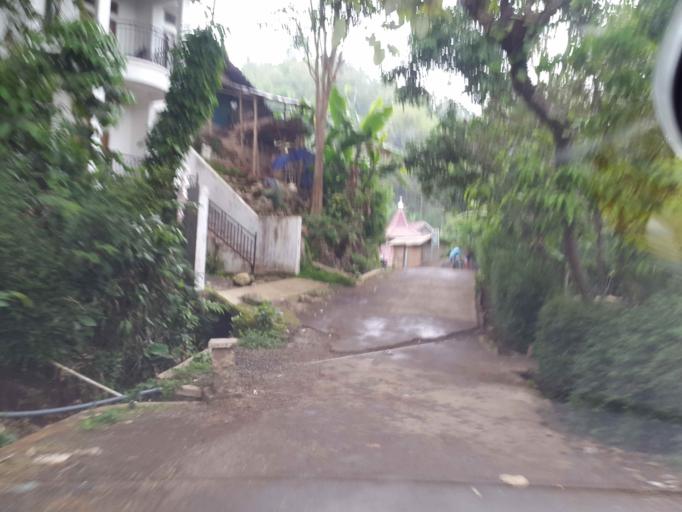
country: ID
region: Central Java
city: Margasari
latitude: -7.1895
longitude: 109.0801
